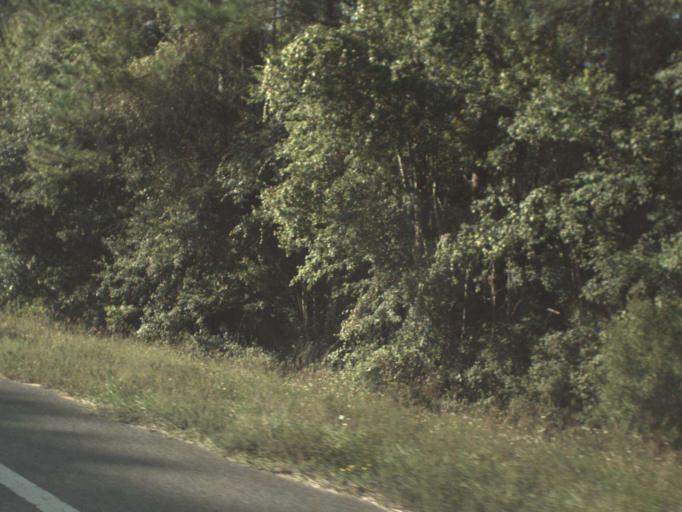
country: US
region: Florida
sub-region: Bay County
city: Laguna Beach
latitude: 30.4476
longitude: -85.8398
